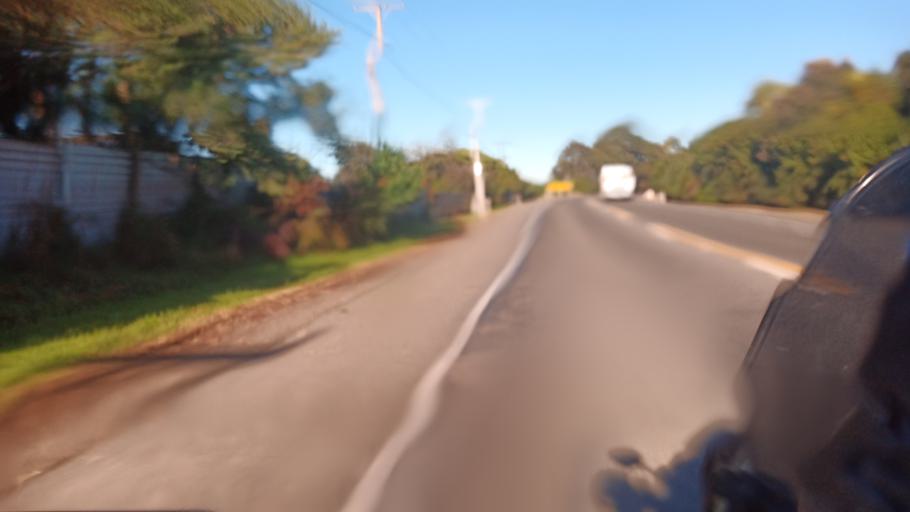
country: NZ
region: Hawke's Bay
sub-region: Napier City
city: Napier
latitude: -39.3817
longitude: 176.8907
